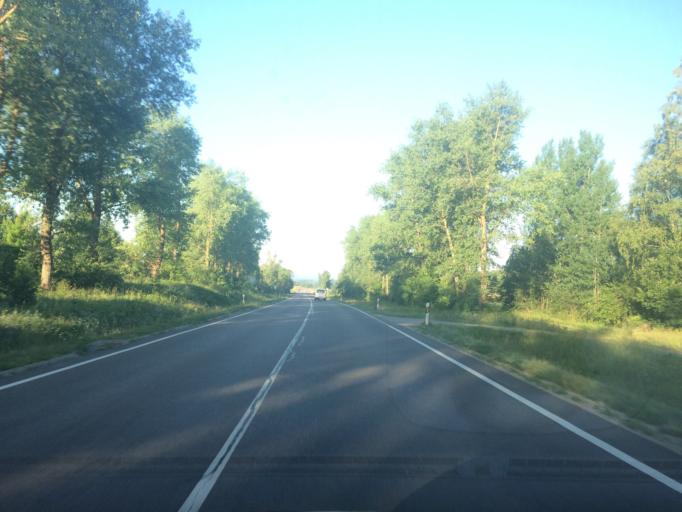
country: LT
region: Utenos apskritis
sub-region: Anyksciai
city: Anyksciai
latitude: 55.4237
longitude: 25.2269
